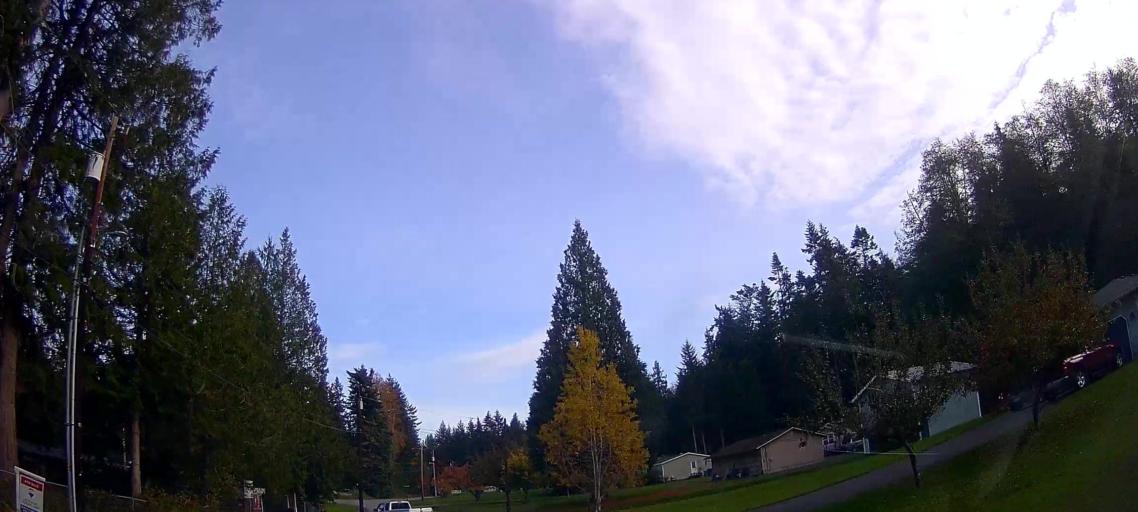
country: US
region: Washington
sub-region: Snohomish County
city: Stanwood
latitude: 48.2804
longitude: -122.3465
